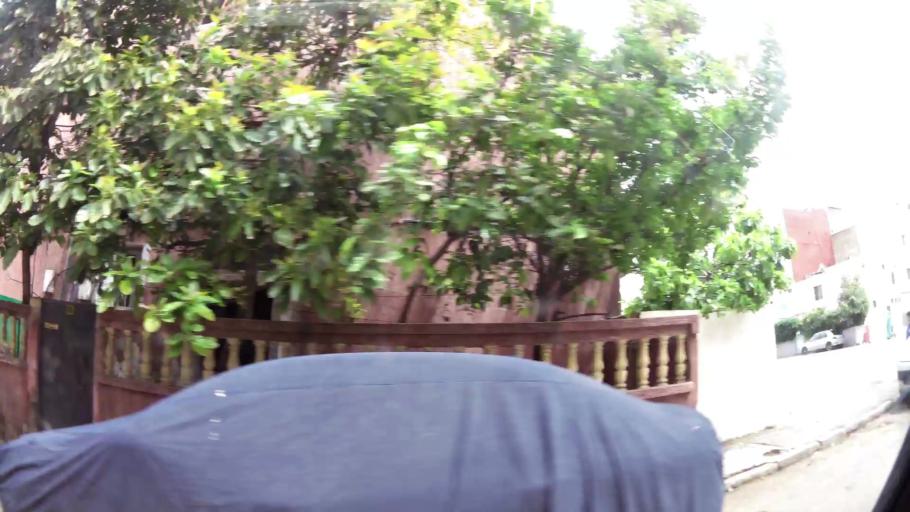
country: MA
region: Grand Casablanca
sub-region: Mediouna
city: Tit Mellil
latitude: 33.6078
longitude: -7.5119
